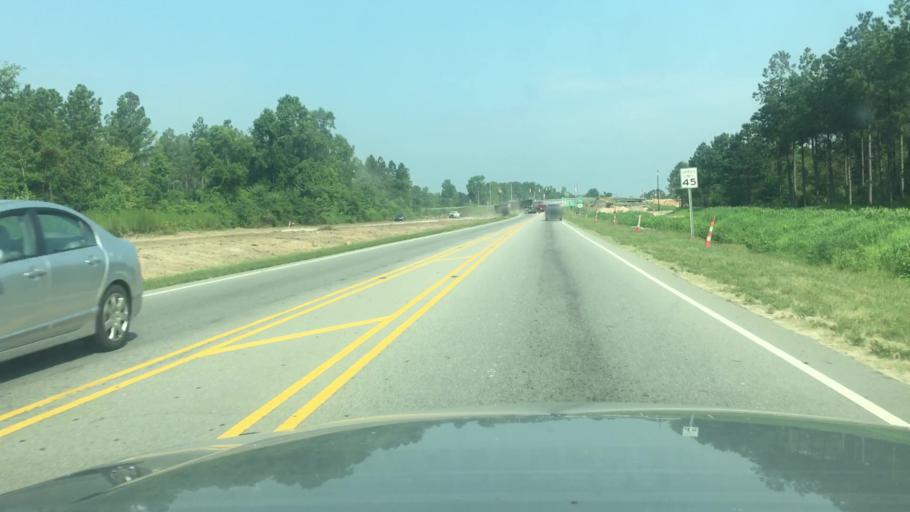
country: US
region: North Carolina
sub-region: Cumberland County
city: Hope Mills
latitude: 34.9421
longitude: -78.9269
